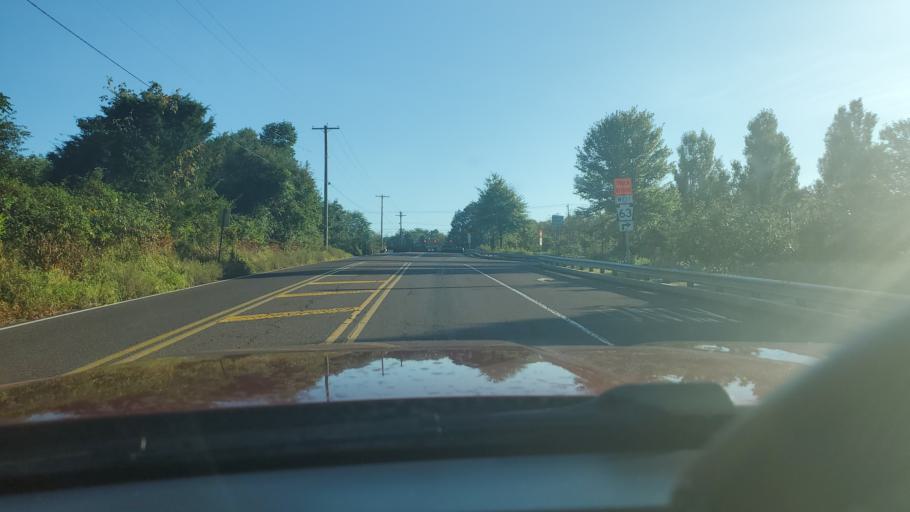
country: US
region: Pennsylvania
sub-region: Montgomery County
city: Harleysville
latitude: 40.2993
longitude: -75.4152
